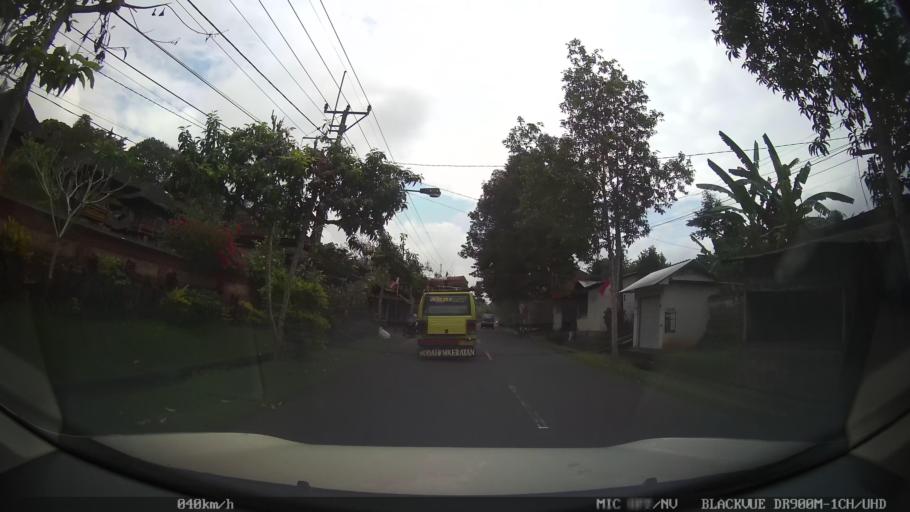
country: ID
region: Bali
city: Banjar Bebalang
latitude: -8.4898
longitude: 115.3494
